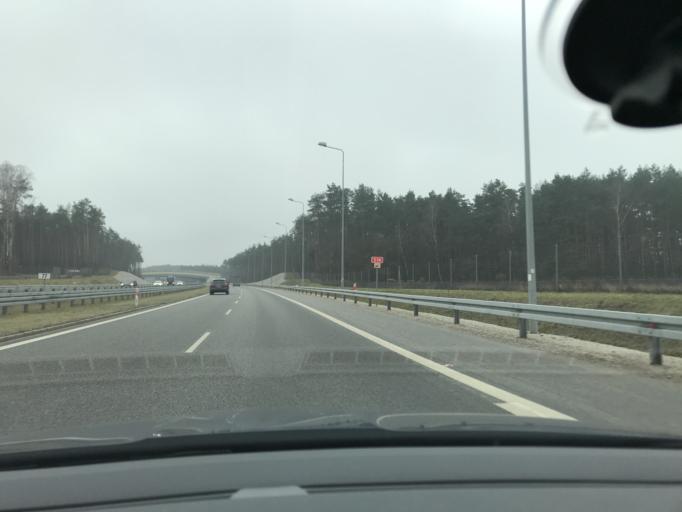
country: PL
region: Lodz Voivodeship
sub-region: Powiat pabianicki
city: Dobron
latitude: 51.6333
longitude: 19.2705
